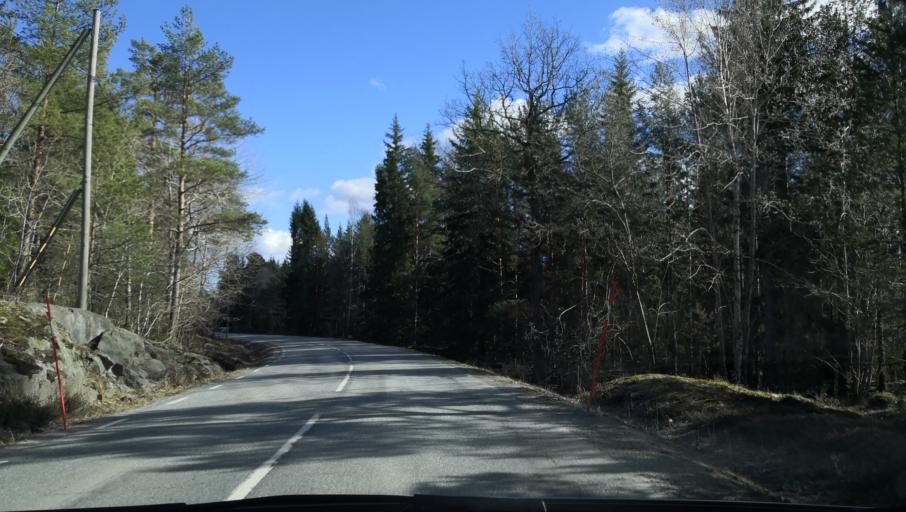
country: SE
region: Stockholm
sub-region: Varmdo Kommun
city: Hemmesta
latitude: 59.3612
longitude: 18.5365
